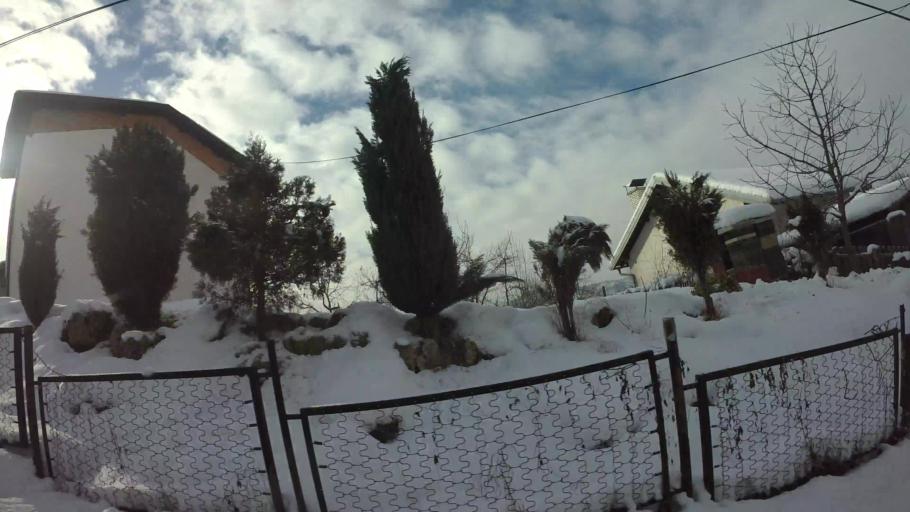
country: BA
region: Federation of Bosnia and Herzegovina
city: Kobilja Glava
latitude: 43.8799
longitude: 18.4171
